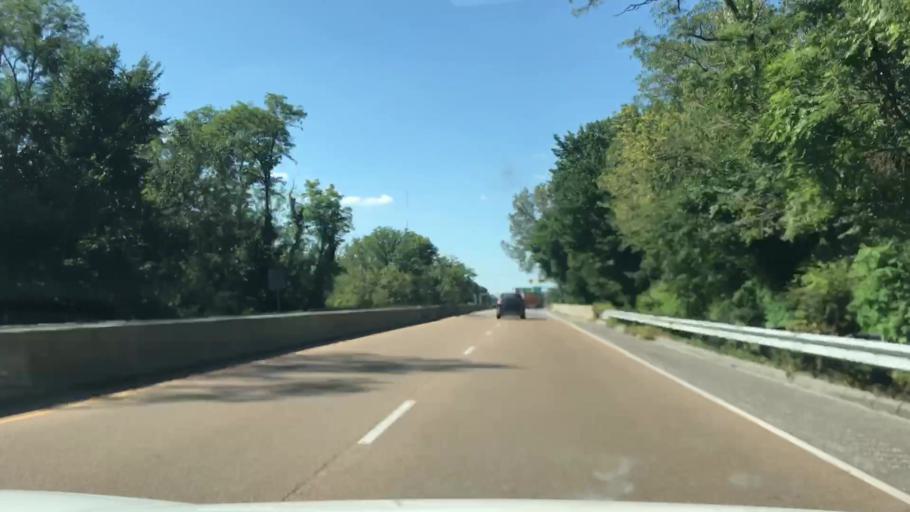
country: US
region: Illinois
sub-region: Saint Clair County
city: Alorton
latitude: 38.5588
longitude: -90.0816
